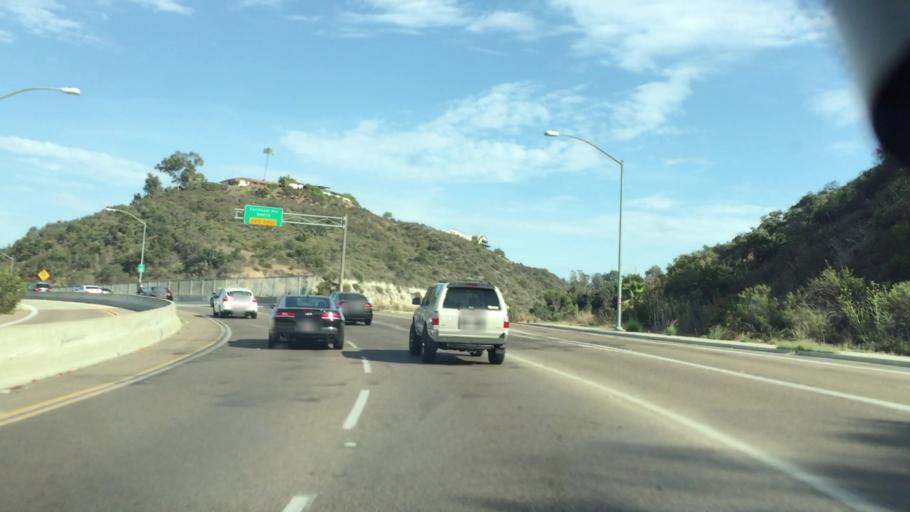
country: US
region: California
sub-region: San Diego County
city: Lemon Grove
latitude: 32.7730
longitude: -117.0980
